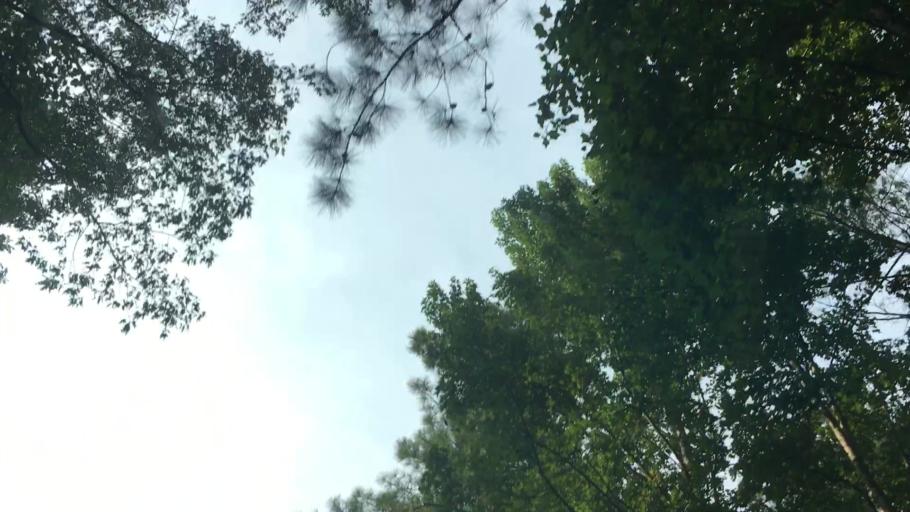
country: US
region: Alabama
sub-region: Bibb County
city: Woodstock
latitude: 33.2334
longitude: -87.1437
